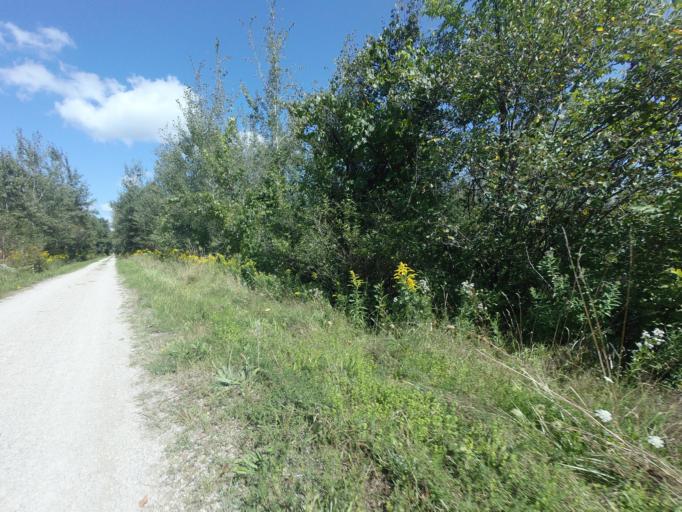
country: CA
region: Ontario
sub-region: Wellington County
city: Guelph
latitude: 43.7473
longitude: -80.3176
